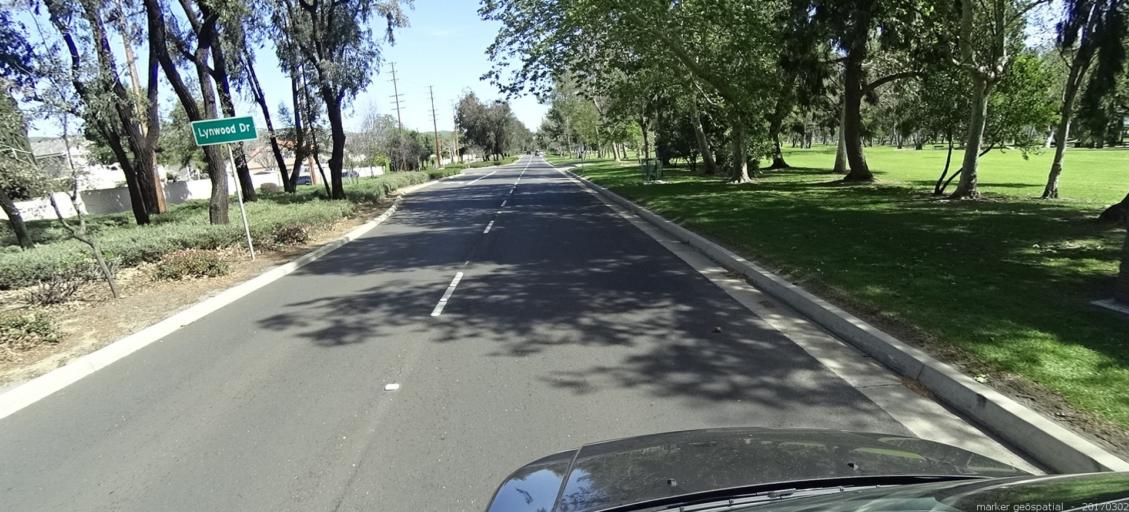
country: US
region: California
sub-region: Orange County
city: Yorba Linda
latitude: 33.8723
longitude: -117.7610
